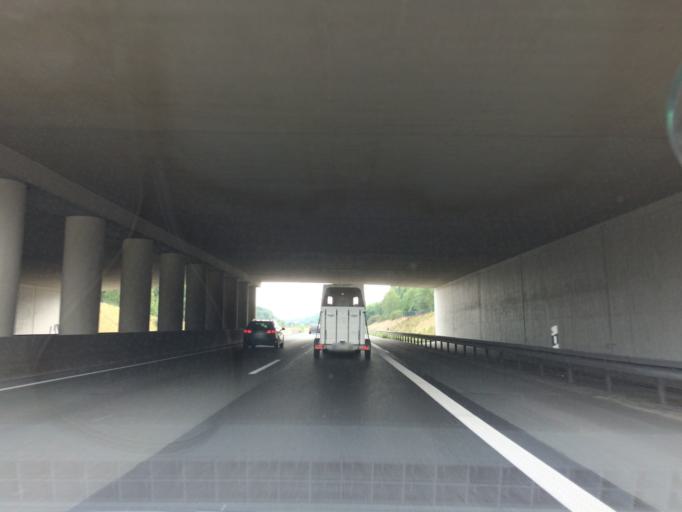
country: DE
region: North Rhine-Westphalia
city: Dorsten
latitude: 51.7178
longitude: 6.9329
